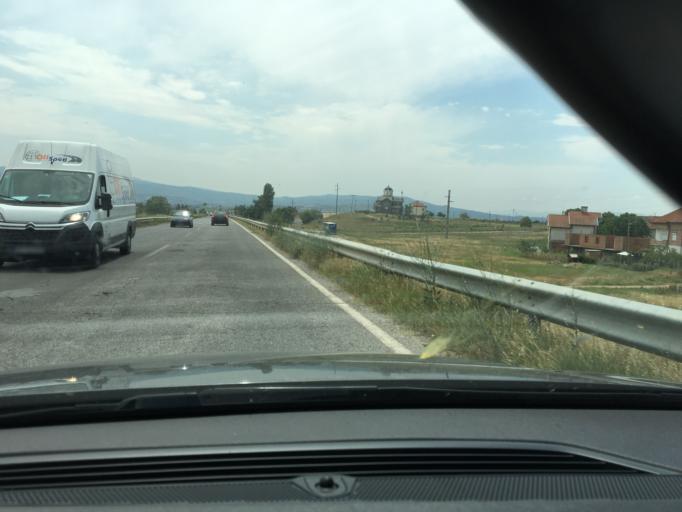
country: MK
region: Stip
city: Shtip
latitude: 41.7765
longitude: 22.1341
